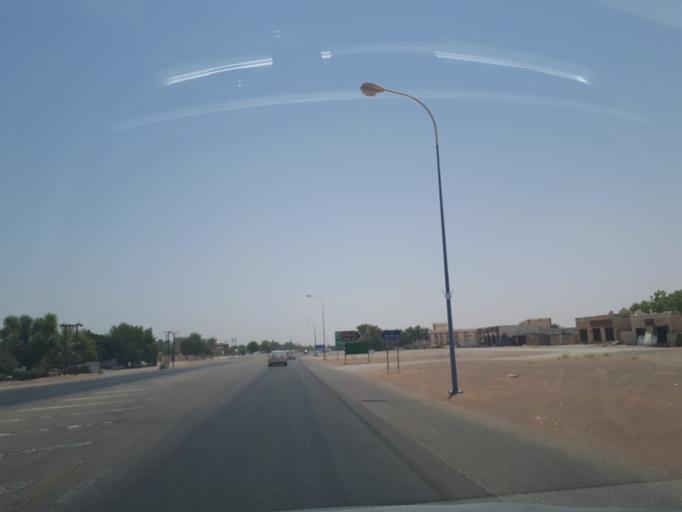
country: OM
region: Ash Sharqiyah
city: Badiyah
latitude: 22.5060
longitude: 58.7454
